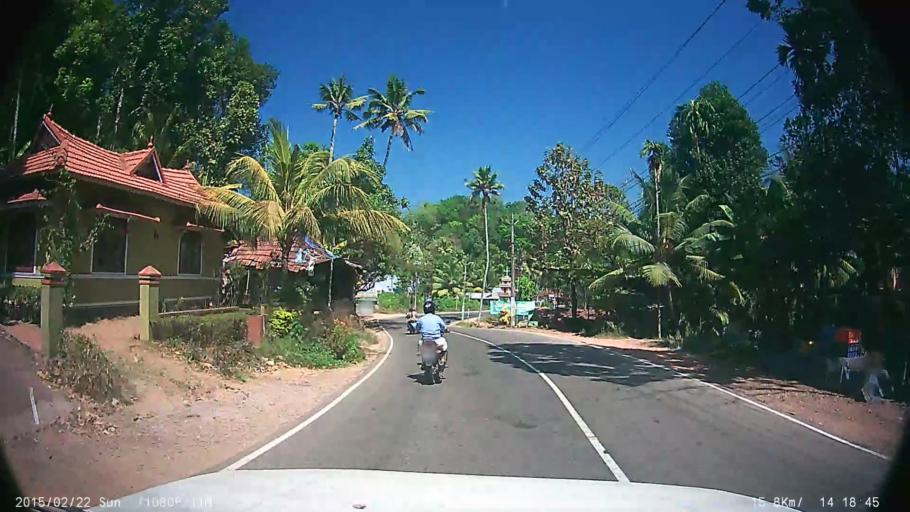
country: IN
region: Kerala
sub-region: Kottayam
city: Lalam
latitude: 9.5670
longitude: 76.6872
